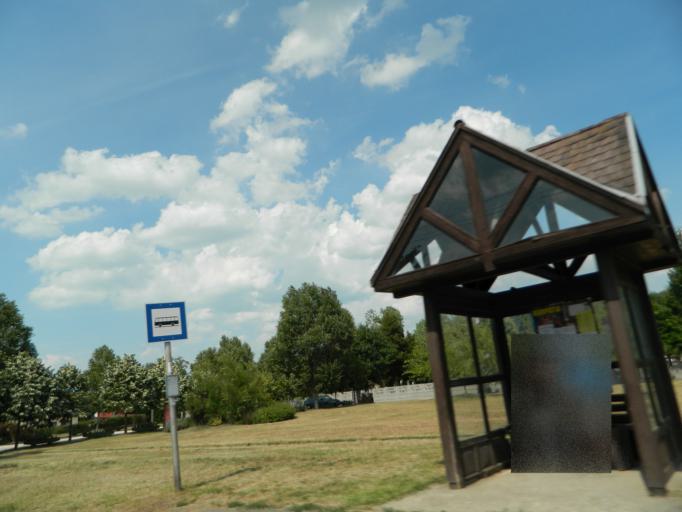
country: HU
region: Somogy
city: Balatonfoldvar
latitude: 46.8218
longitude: 17.9056
